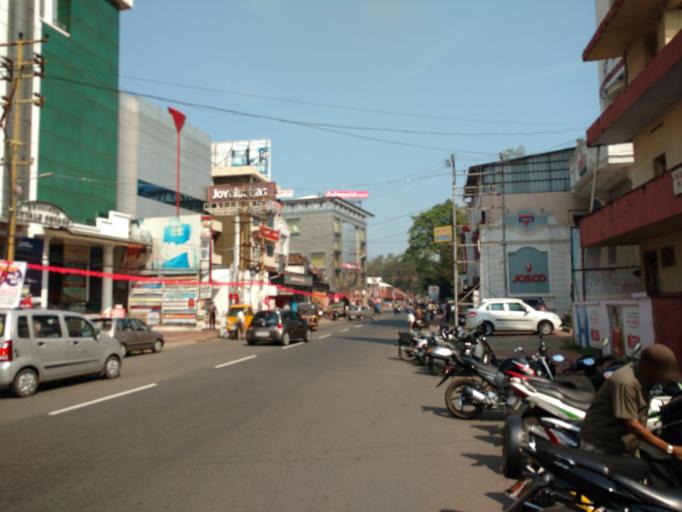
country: IN
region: Kerala
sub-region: Thrissur District
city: Trichur
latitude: 10.5282
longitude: 76.2182
